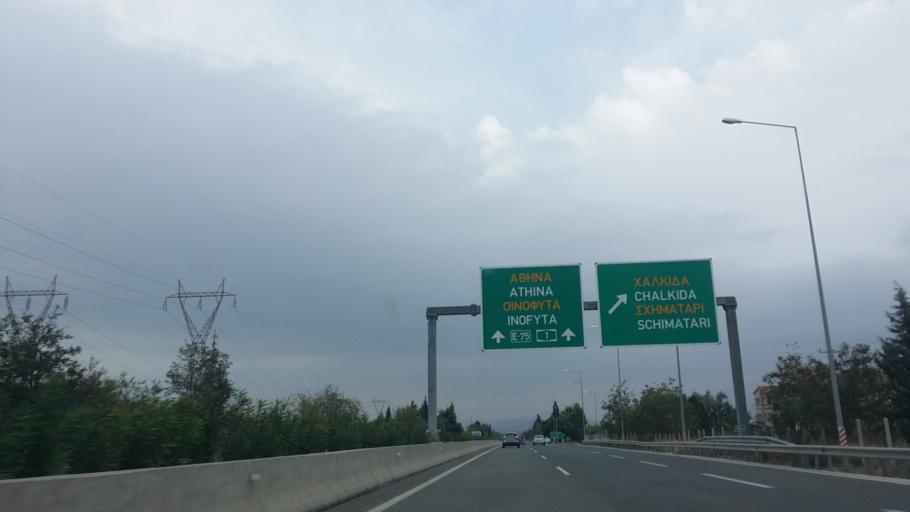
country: GR
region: Central Greece
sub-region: Nomos Voiotias
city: Schimatari
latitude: 38.3572
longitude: 23.5648
